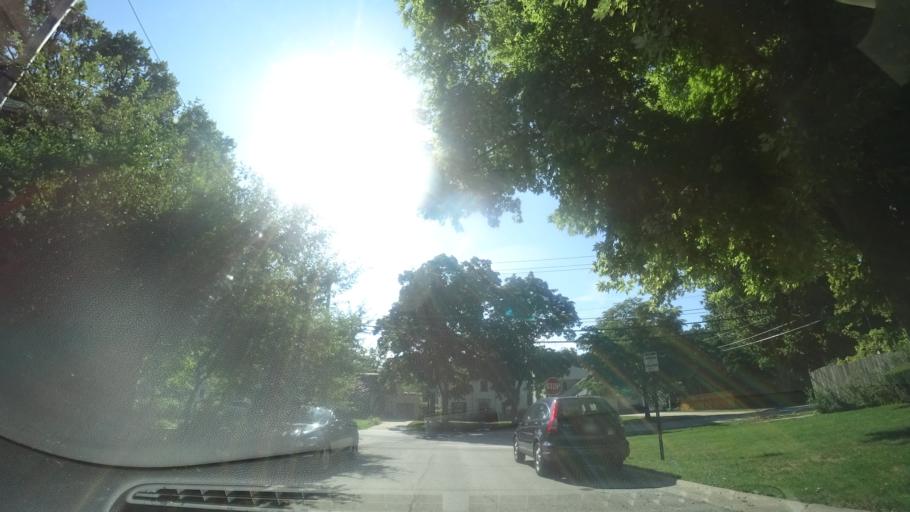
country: US
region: Illinois
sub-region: Cook County
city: Wilmette
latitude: 42.0547
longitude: -87.7089
